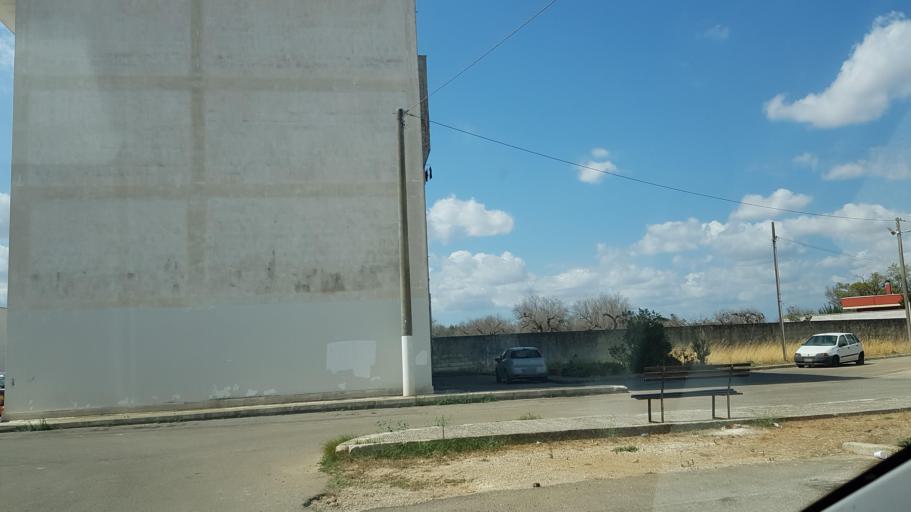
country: IT
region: Apulia
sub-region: Provincia di Lecce
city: Trepuzzi
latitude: 40.4096
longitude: 18.0633
